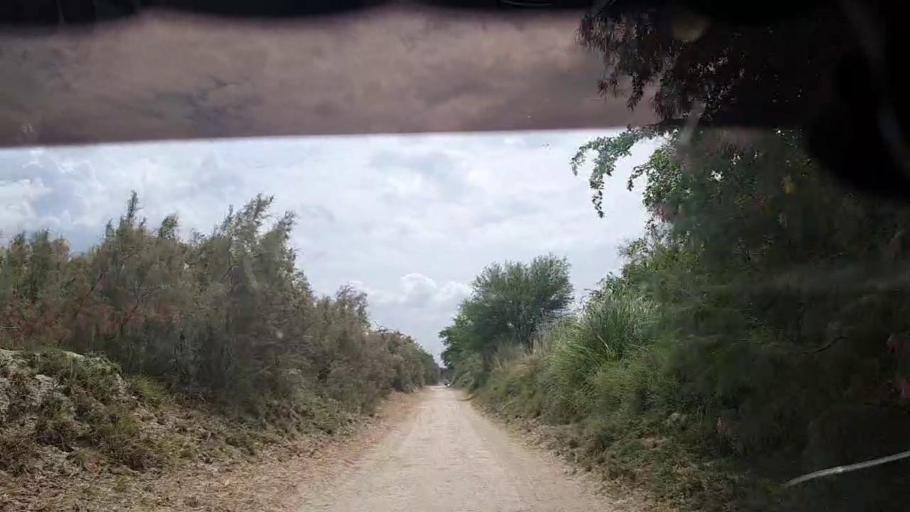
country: PK
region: Sindh
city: Rustam jo Goth
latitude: 28.0442
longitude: 68.9420
